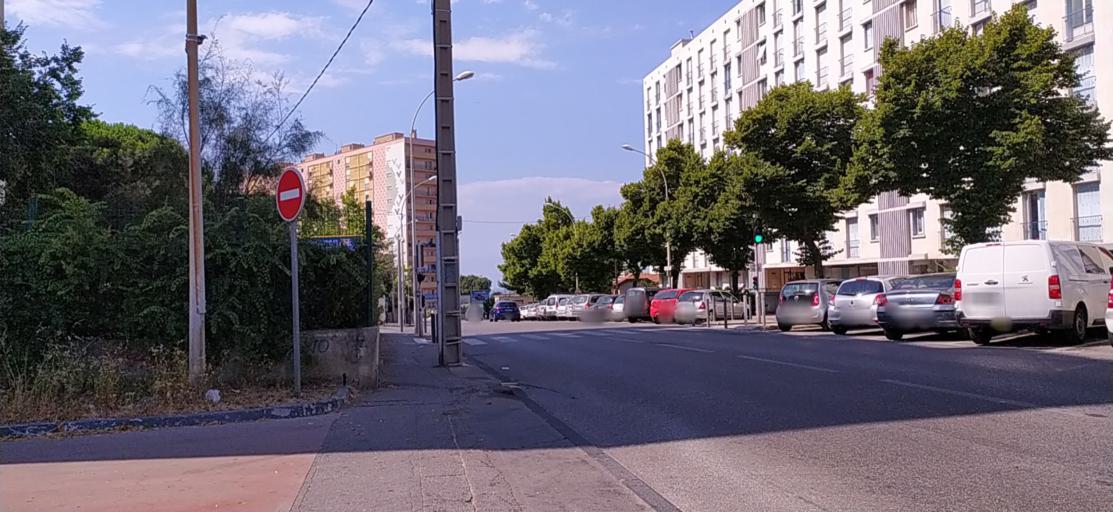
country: FR
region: Provence-Alpes-Cote d'Azur
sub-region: Departement des Bouches-du-Rhone
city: Marseille 16
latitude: 43.3458
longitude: 5.3548
